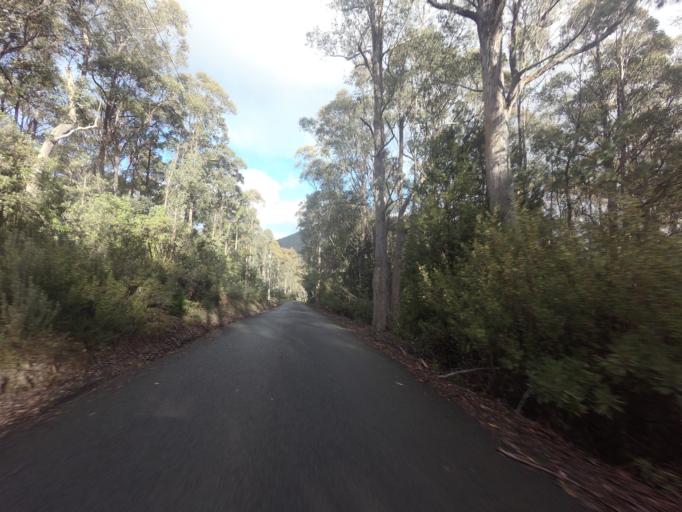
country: AU
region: Tasmania
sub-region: Glenorchy
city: Berriedale
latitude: -42.8438
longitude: 147.1478
